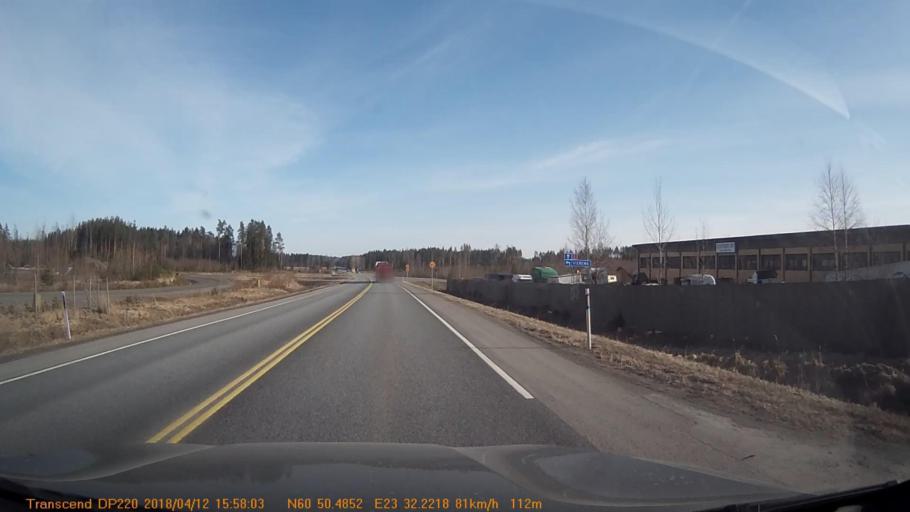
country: FI
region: Haeme
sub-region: Forssa
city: Jokioinen
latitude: 60.8408
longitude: 23.5383
